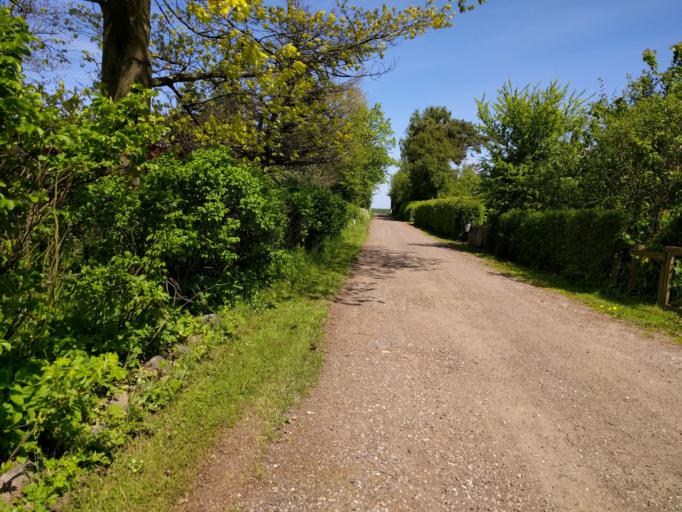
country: DK
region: Zealand
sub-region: Guldborgsund Kommune
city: Stubbekobing
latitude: 54.7455
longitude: 12.0318
